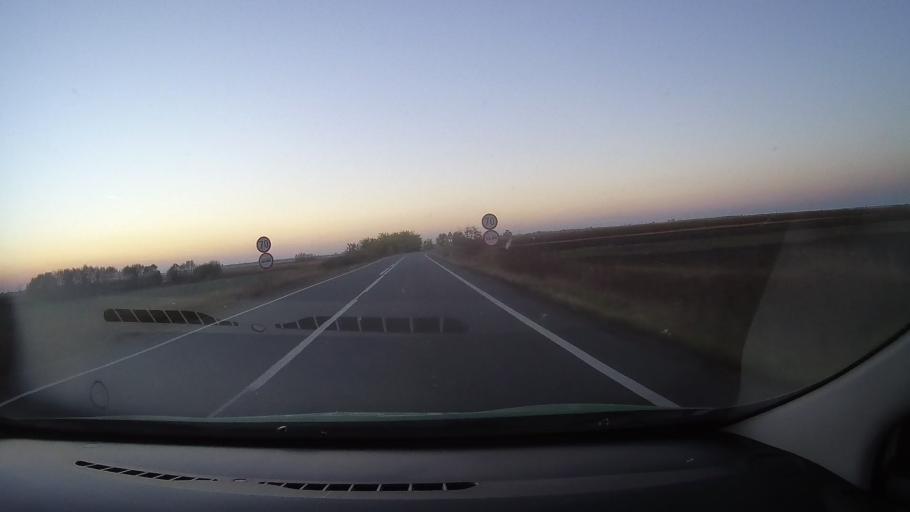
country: RO
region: Bihor
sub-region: Comuna Tarcea
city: Tarcea
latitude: 47.4391
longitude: 22.1949
